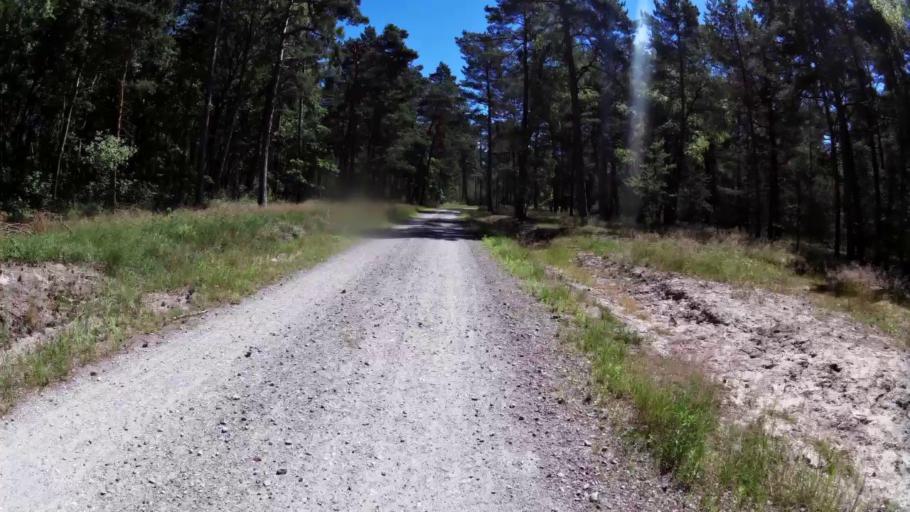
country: PL
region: West Pomeranian Voivodeship
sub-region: Powiat gryficki
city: Cerkwica
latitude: 54.0975
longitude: 15.1457
